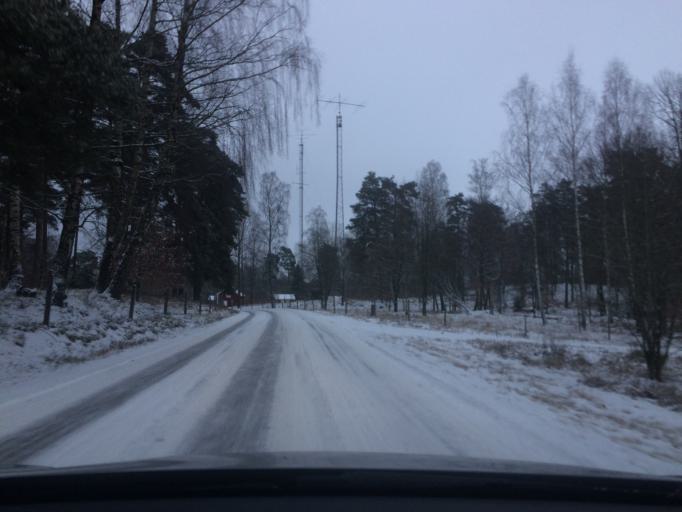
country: SE
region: Kronoberg
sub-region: Vaxjo Kommun
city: Vaexjoe
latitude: 56.8567
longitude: 14.7630
